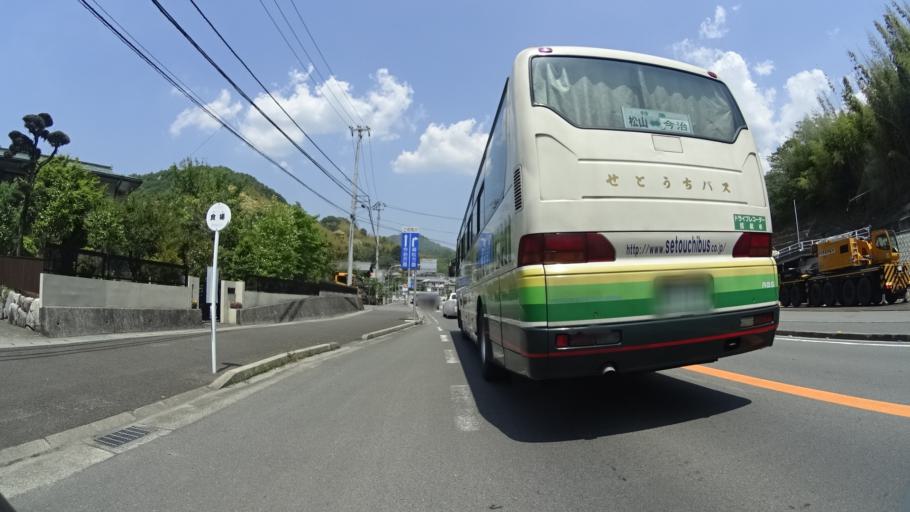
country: JP
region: Ehime
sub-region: Shikoku-chuo Shi
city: Matsuyama
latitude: 33.8619
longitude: 132.8167
